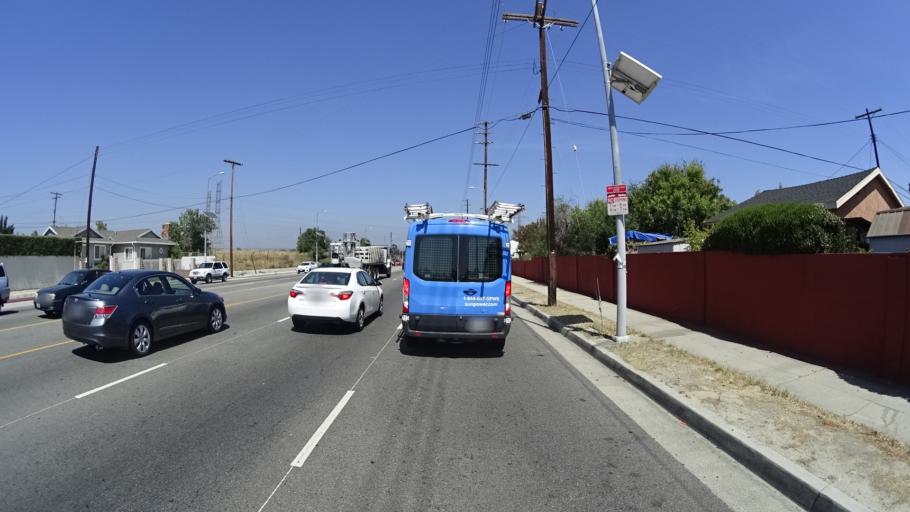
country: US
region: California
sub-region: Los Angeles County
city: Van Nuys
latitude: 34.2216
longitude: -118.4171
